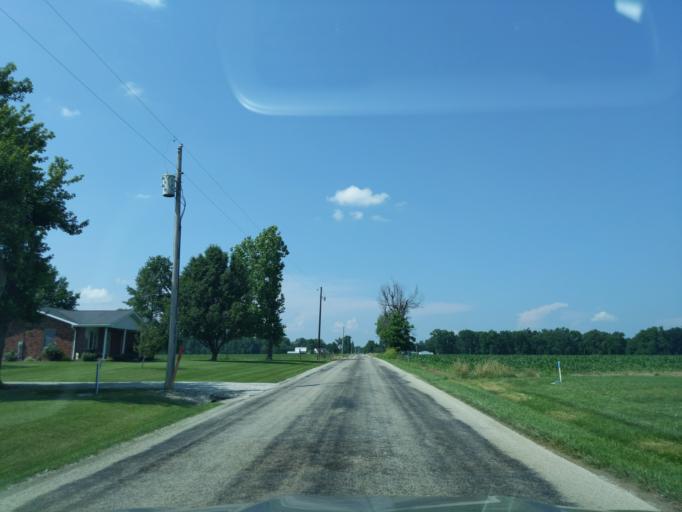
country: US
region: Indiana
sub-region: Ripley County
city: Osgood
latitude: 39.0766
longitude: -85.3486
